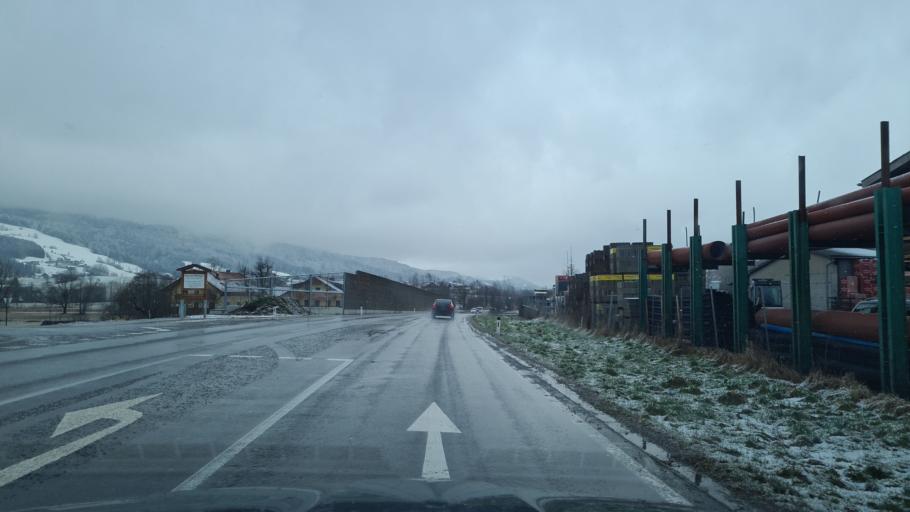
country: AT
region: Upper Austria
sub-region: Politischer Bezirk Vocklabruck
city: Zell am Moos
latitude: 47.8727
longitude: 13.3225
